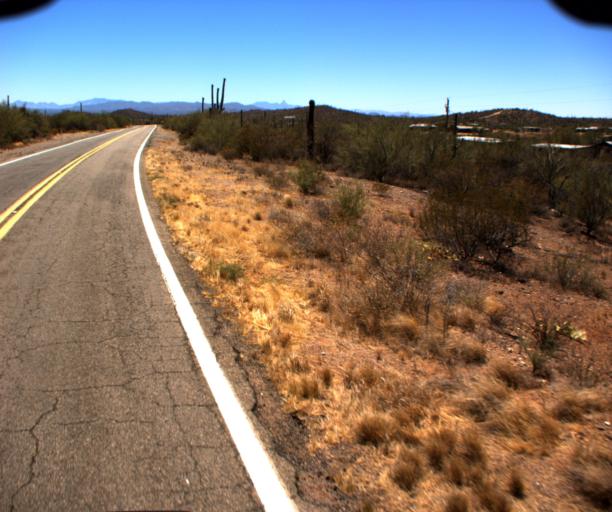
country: US
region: Arizona
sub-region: Pima County
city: Sells
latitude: 32.1680
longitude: -112.1293
